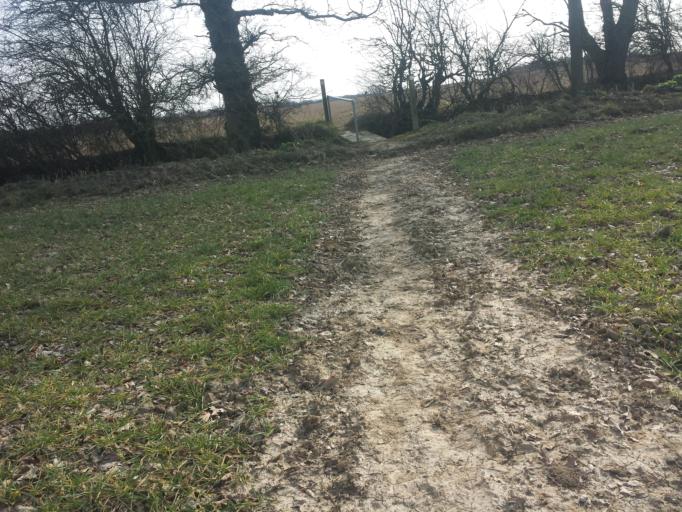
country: GB
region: England
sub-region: Essex
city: Little Clacton
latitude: 51.9032
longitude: 1.1530
